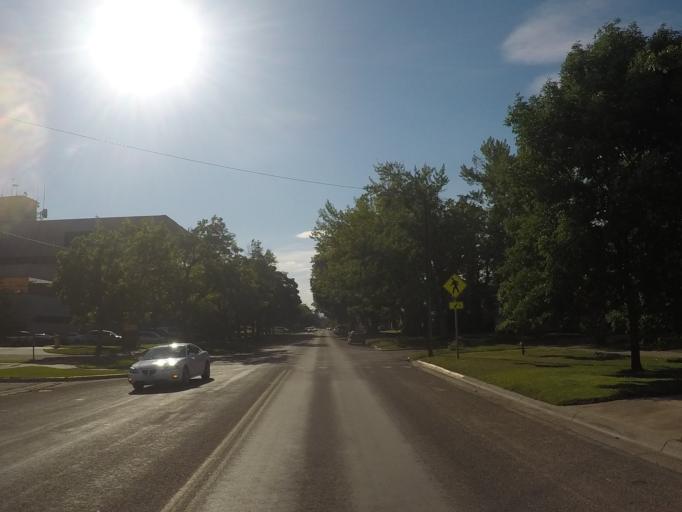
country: US
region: Montana
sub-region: Missoula County
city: Missoula
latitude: 46.8757
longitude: -113.9982
